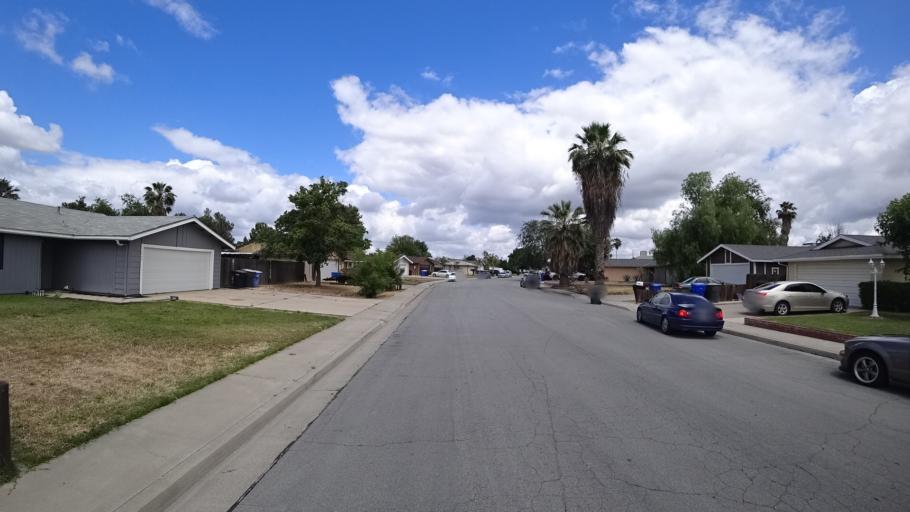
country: US
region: California
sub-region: Kings County
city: Hanford
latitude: 36.3401
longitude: -119.6256
